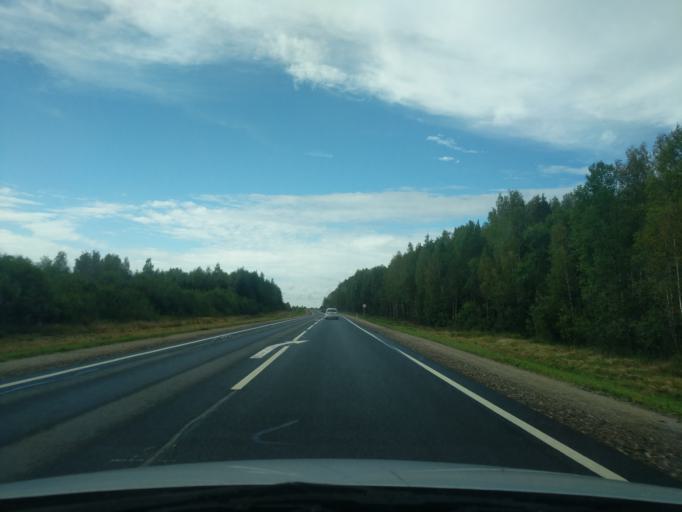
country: RU
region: Kostroma
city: Ostrovskoye
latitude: 57.8148
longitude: 41.9749
